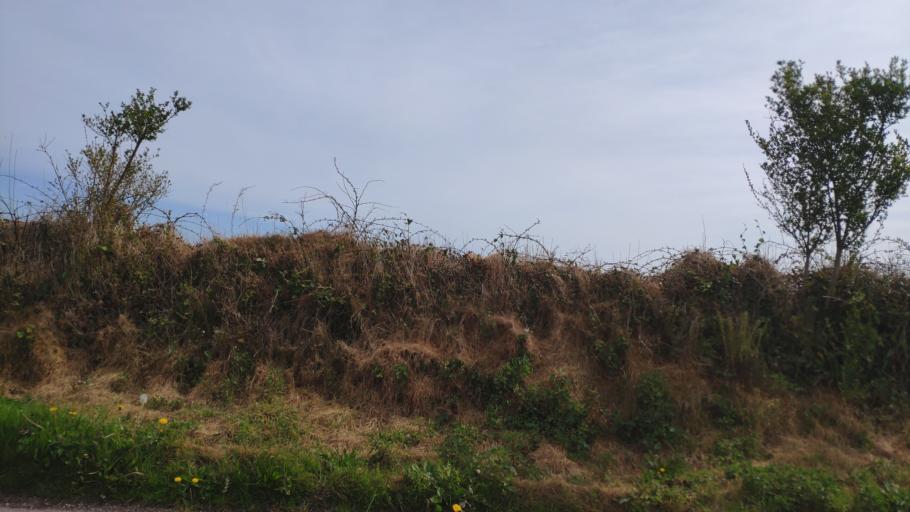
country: IE
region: Munster
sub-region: County Cork
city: Blarney
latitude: 51.9609
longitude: -8.5133
